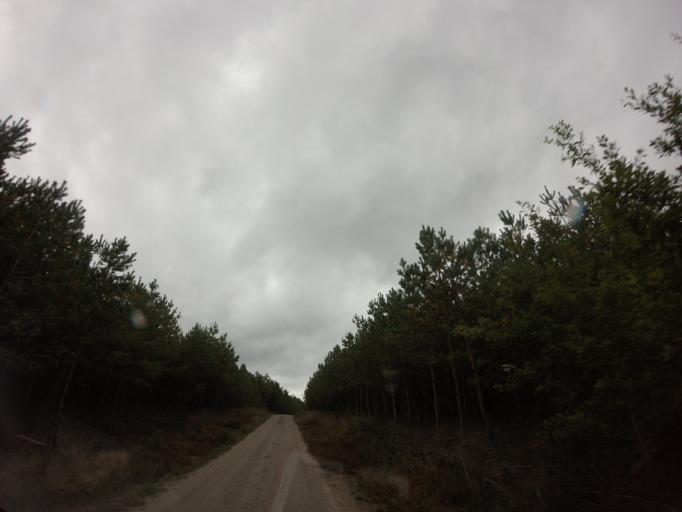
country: PL
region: West Pomeranian Voivodeship
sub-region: Powiat choszczenski
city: Drawno
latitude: 53.1619
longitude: 15.7541
